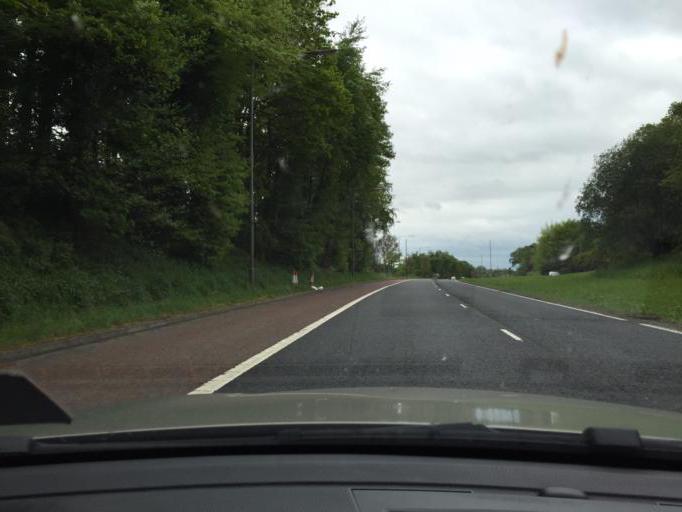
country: GB
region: Northern Ireland
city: Hillsborough
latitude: 54.4785
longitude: -6.0707
